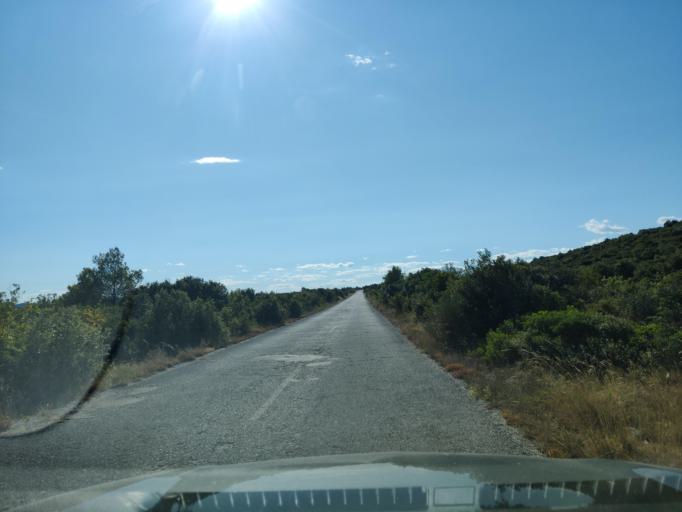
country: HR
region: Sibensko-Kniniska
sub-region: Grad Sibenik
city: Sibenik
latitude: 43.7393
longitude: 15.8648
